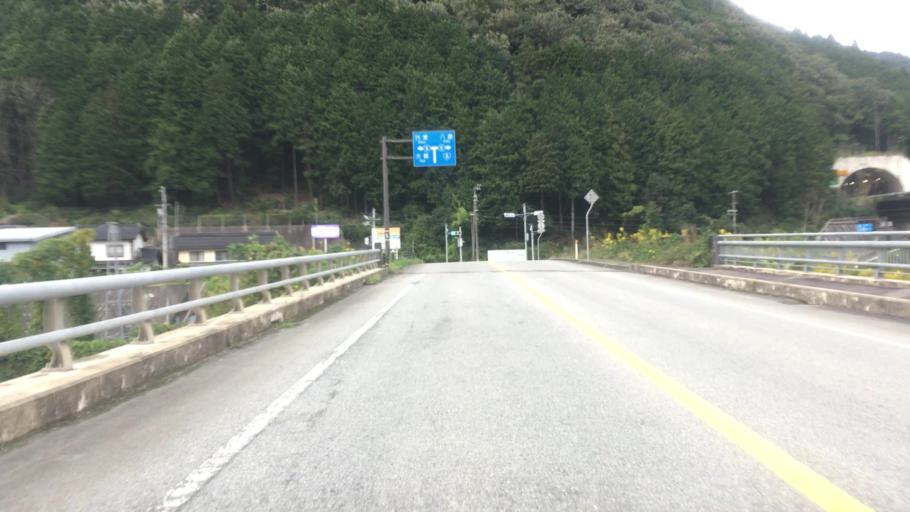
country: JP
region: Hyogo
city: Toyooka
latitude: 35.3616
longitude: 134.7594
